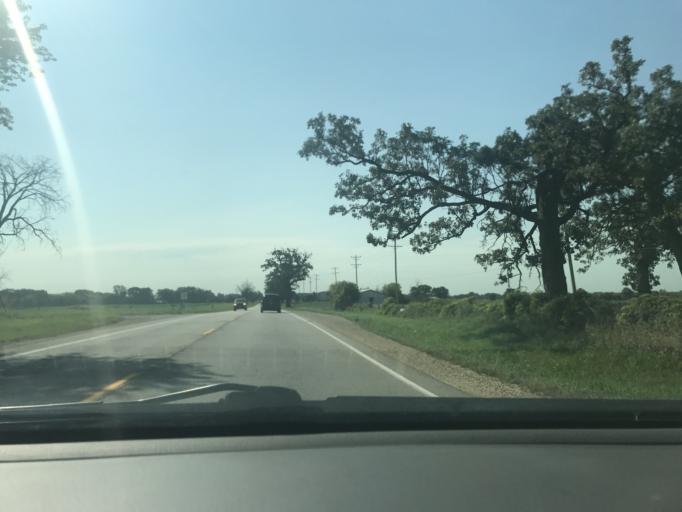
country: US
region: Illinois
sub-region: Kane County
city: Pingree Grove
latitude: 42.0627
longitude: -88.4093
